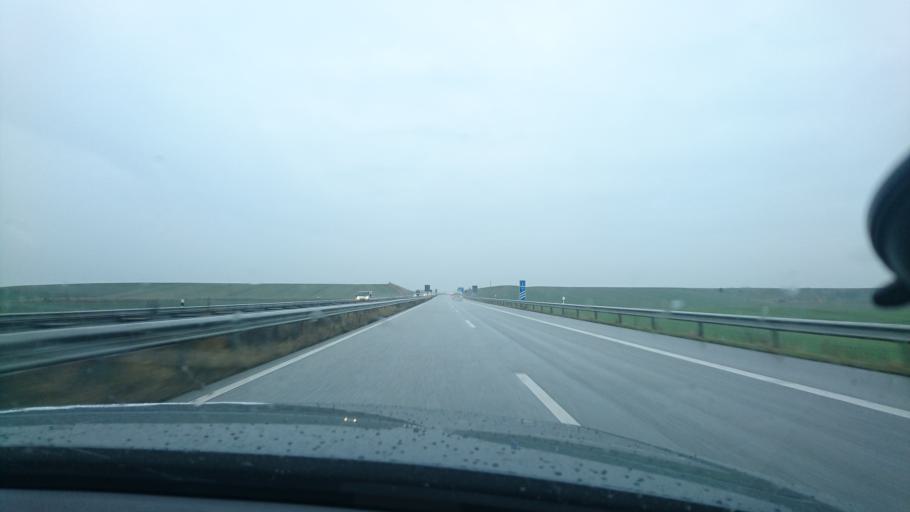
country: DE
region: Schleswig-Holstein
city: Heiligenhafen
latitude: 54.3552
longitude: 10.9569
